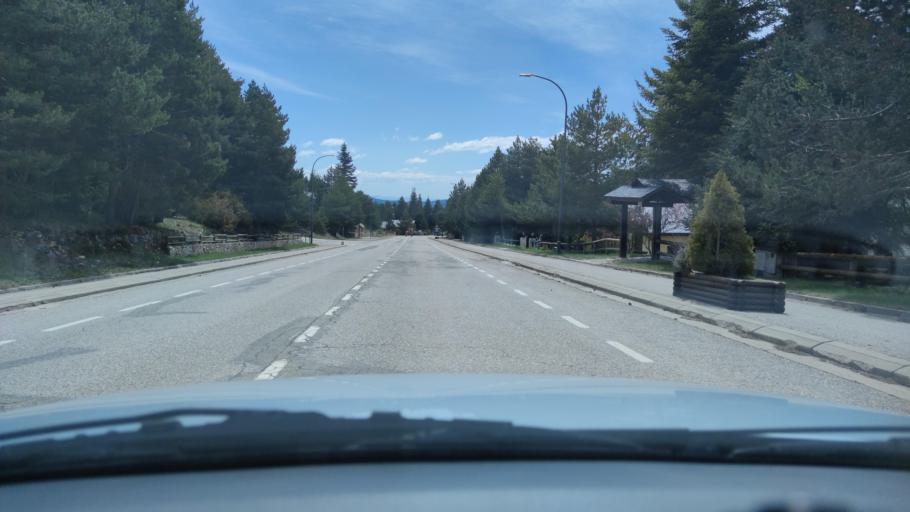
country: ES
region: Catalonia
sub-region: Provincia de Lleida
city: Gosol
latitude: 42.1734
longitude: 1.5664
